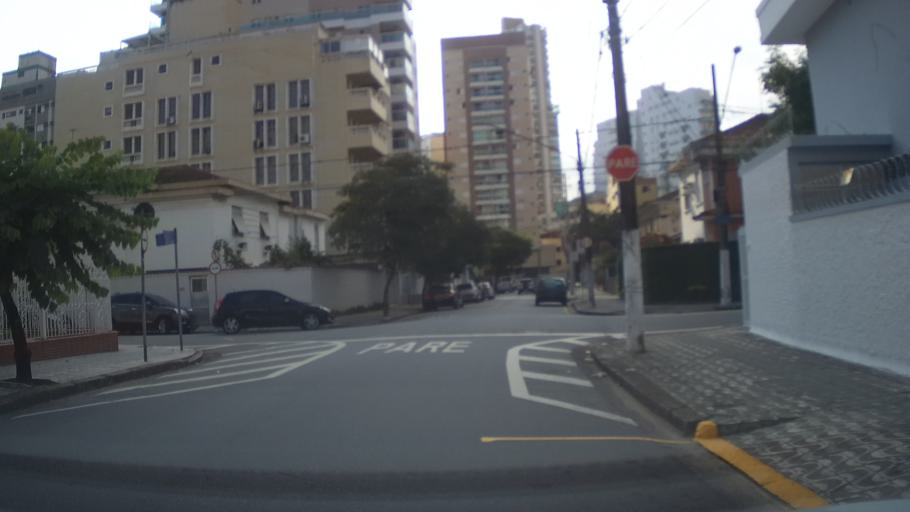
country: BR
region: Sao Paulo
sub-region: Santos
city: Santos
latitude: -23.9711
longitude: -46.3209
